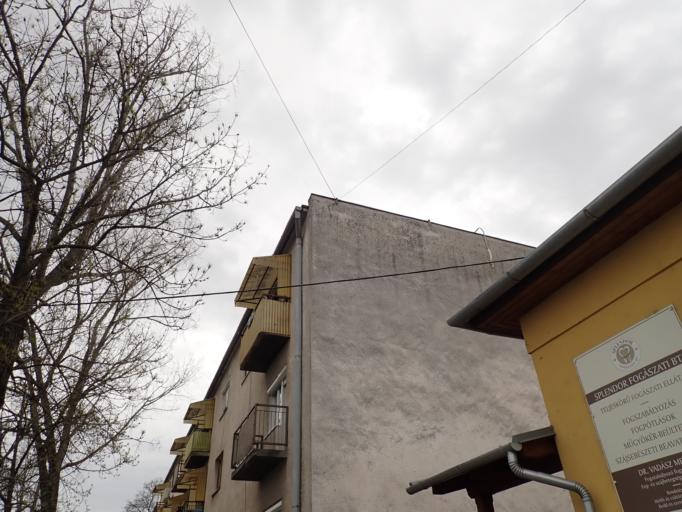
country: HU
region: Tolna
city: Paks
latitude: 46.6181
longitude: 18.8521
